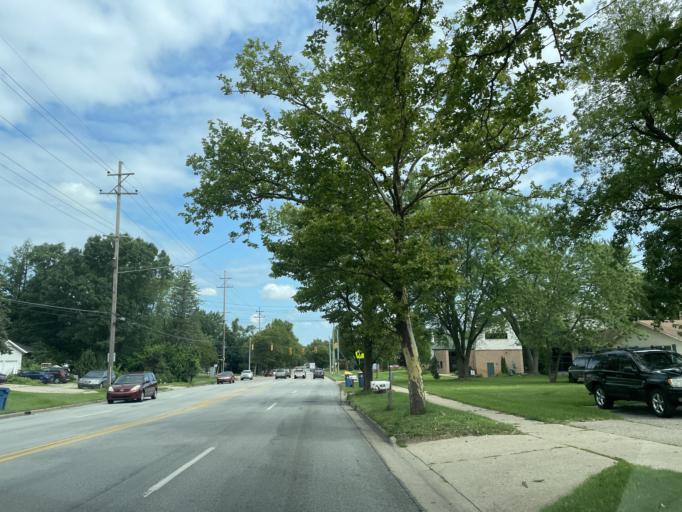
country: US
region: Michigan
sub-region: Kent County
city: Kentwood
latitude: 42.8971
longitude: -85.6266
